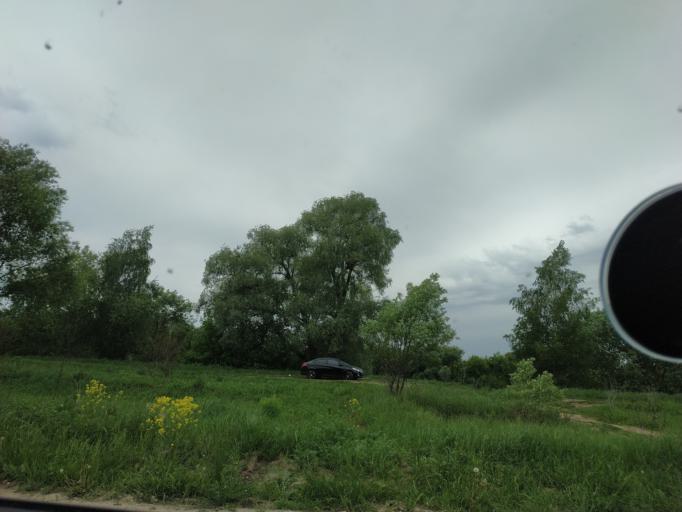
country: RU
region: Moskovskaya
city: Ostrovtsy
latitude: 55.5605
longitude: 38.0298
